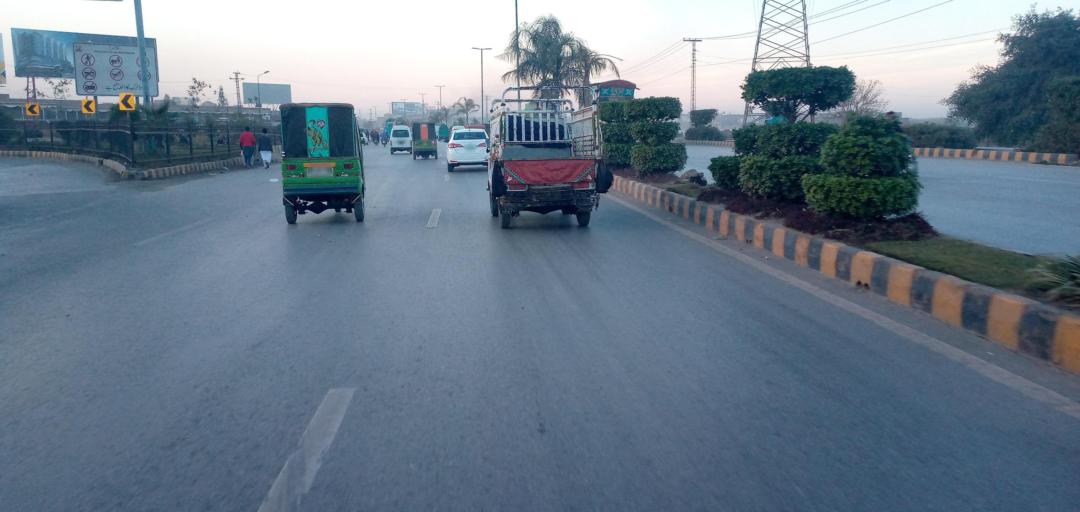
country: PK
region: Khyber Pakhtunkhwa
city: Peshawar
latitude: 34.0263
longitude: 71.6187
